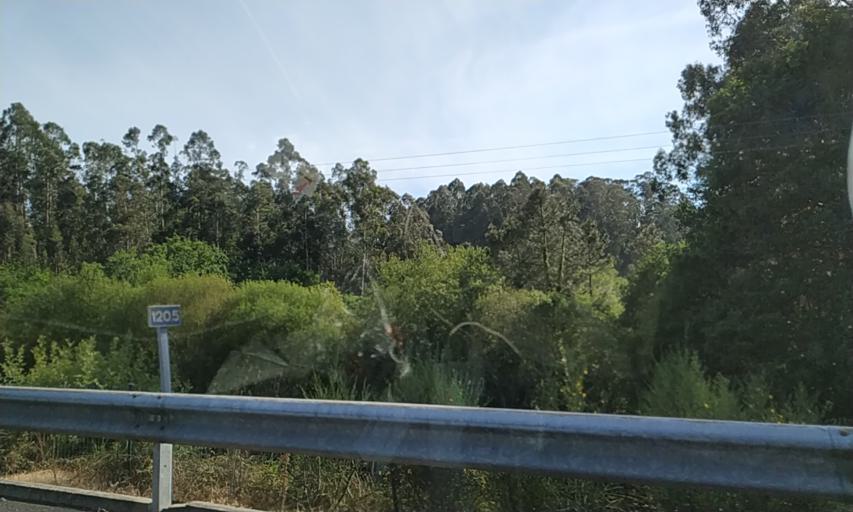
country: ES
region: Galicia
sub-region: Provincia de Pontevedra
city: Barro
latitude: 42.5096
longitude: -8.6595
